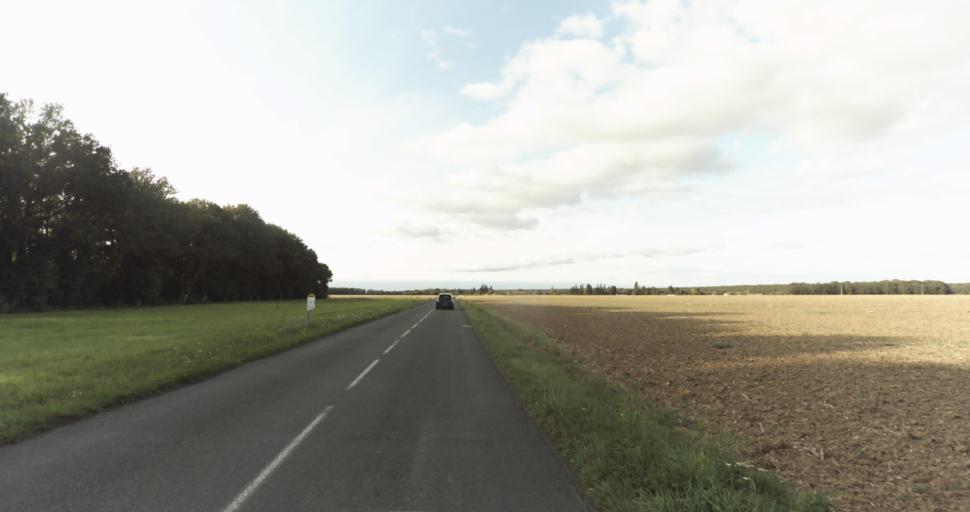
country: FR
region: Haute-Normandie
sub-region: Departement de l'Eure
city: Marcilly-sur-Eure
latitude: 48.8817
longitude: 1.2961
